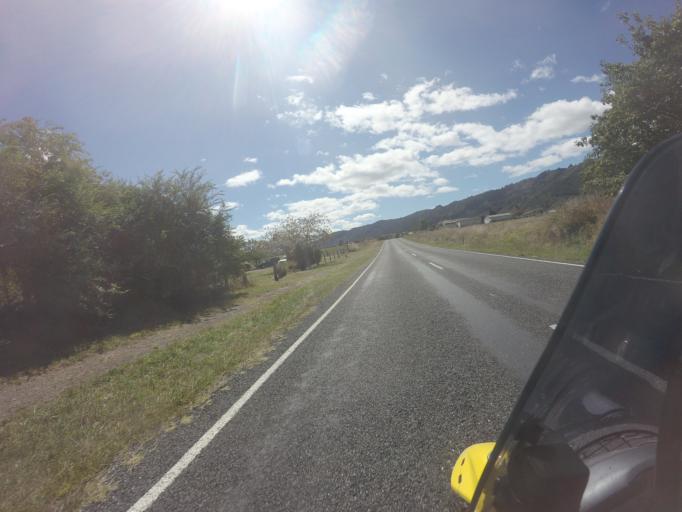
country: NZ
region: Bay of Plenty
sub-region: Kawerau District
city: Kawerau
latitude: -38.2294
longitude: 176.8392
